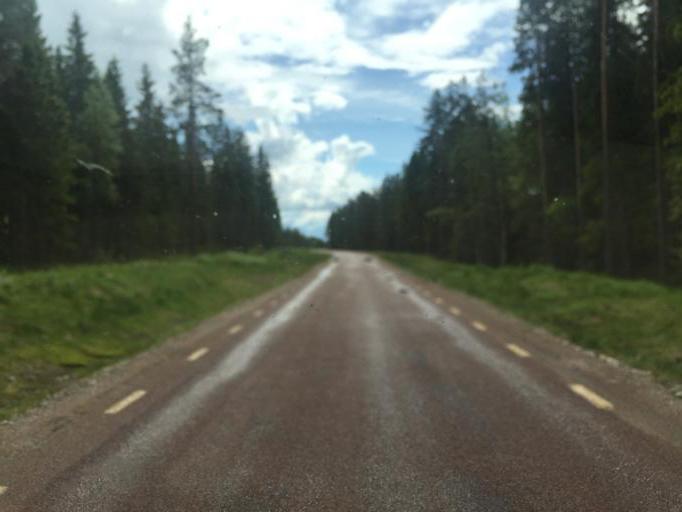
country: SE
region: Dalarna
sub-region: Malung-Saelens kommun
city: Malung
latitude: 60.3496
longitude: 13.8653
